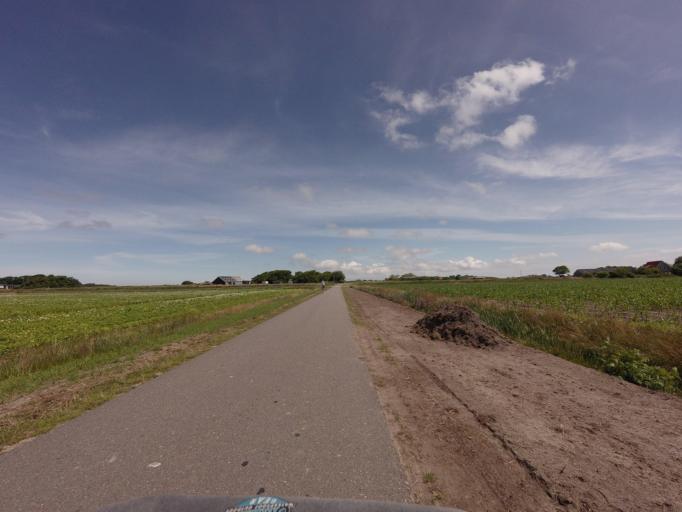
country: NL
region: North Holland
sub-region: Gemeente Texel
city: Den Burg
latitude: 53.0454
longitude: 4.7720
